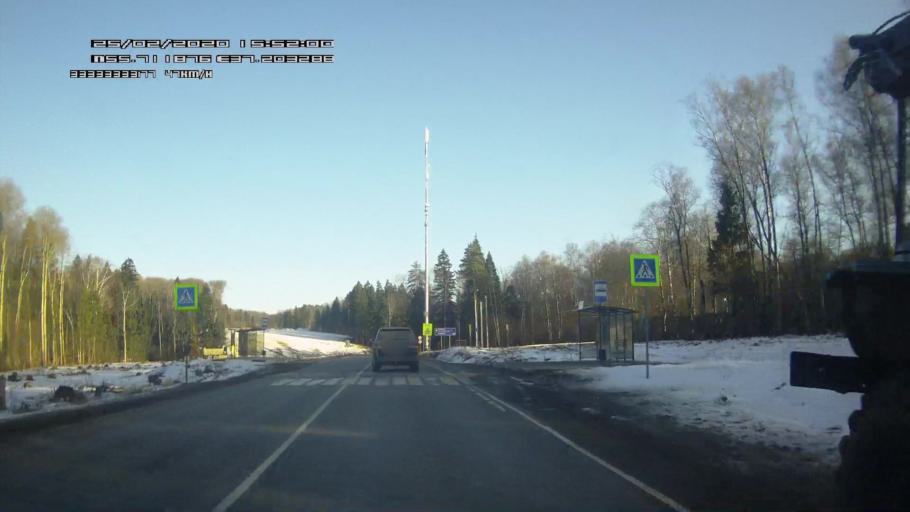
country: RU
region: Moskovskaya
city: Gorki Vtoryye
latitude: 55.7118
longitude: 37.2033
